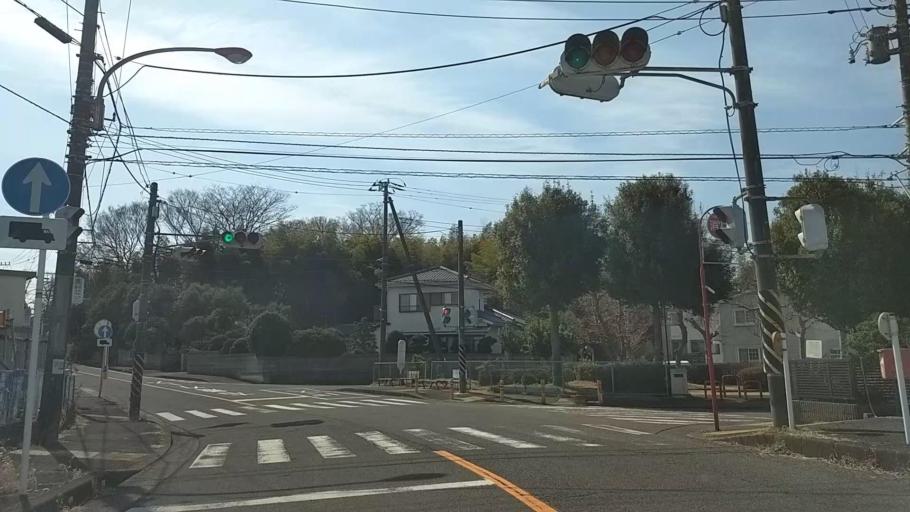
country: JP
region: Kanagawa
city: Fujisawa
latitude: 35.4090
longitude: 139.4551
